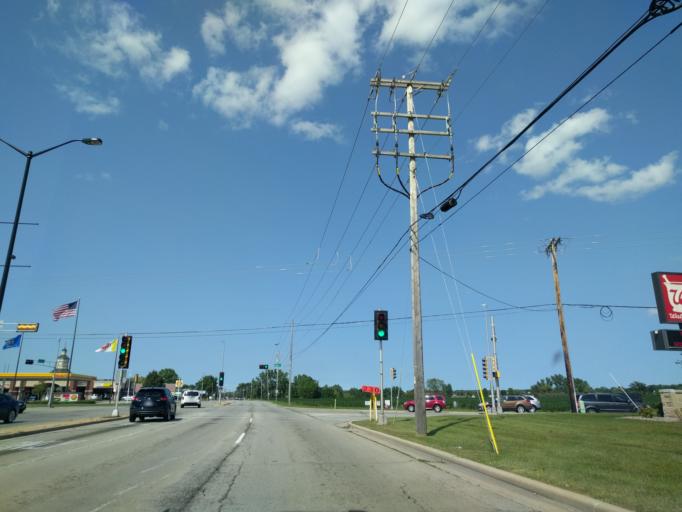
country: US
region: Wisconsin
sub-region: Brown County
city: Allouez
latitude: 44.4650
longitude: -87.9826
